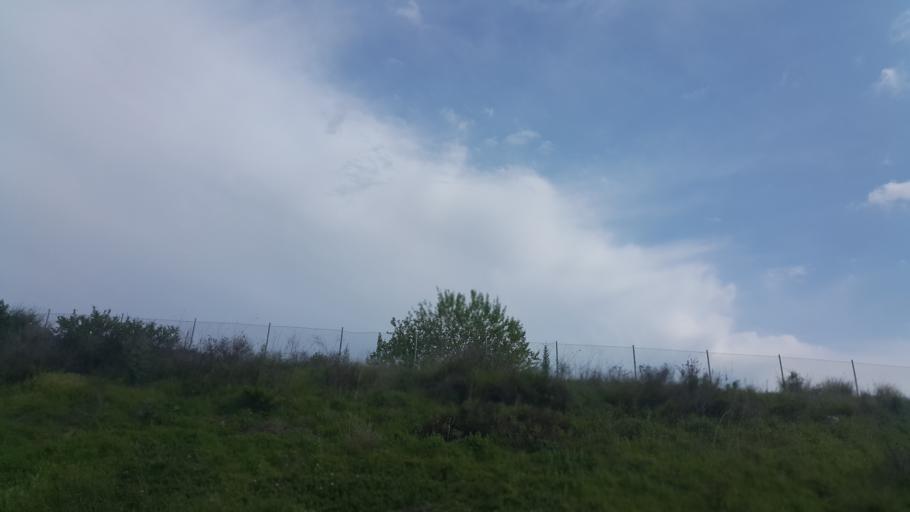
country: TR
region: Mersin
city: Kazanli
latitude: 36.9529
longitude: 34.7410
